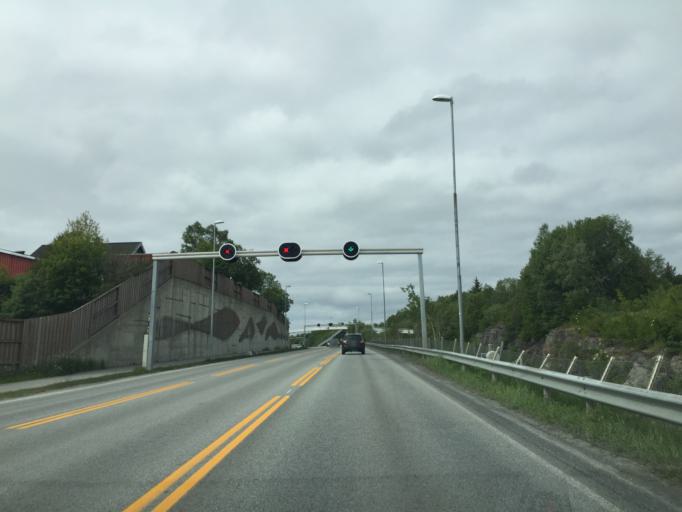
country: NO
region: Nordland
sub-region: Bodo
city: Lopsmarka
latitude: 67.2776
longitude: 14.4941
